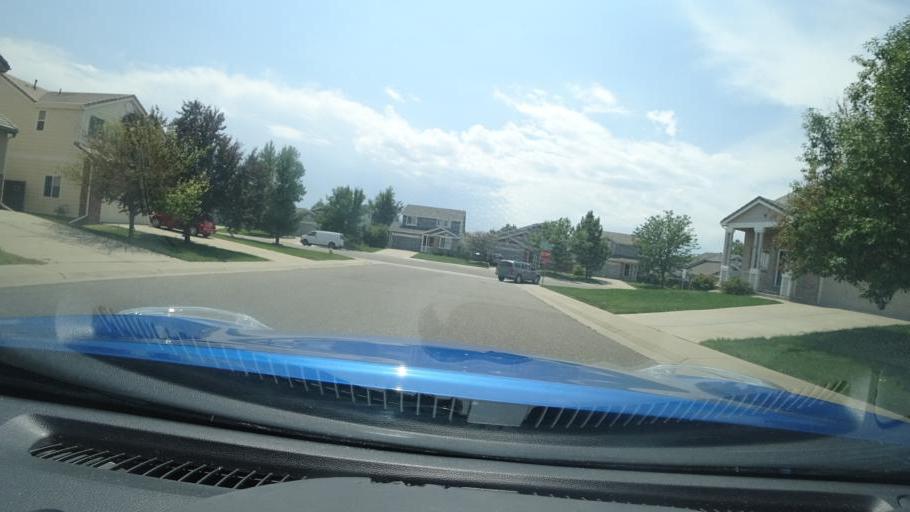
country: US
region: Colorado
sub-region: Adams County
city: Aurora
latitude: 39.6727
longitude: -104.7559
